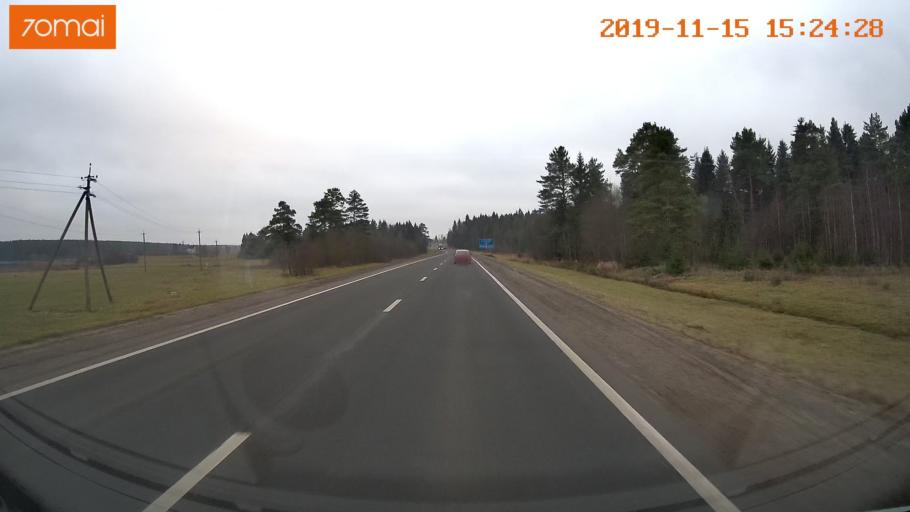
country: RU
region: Jaroslavl
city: Danilov
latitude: 58.1772
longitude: 40.1329
